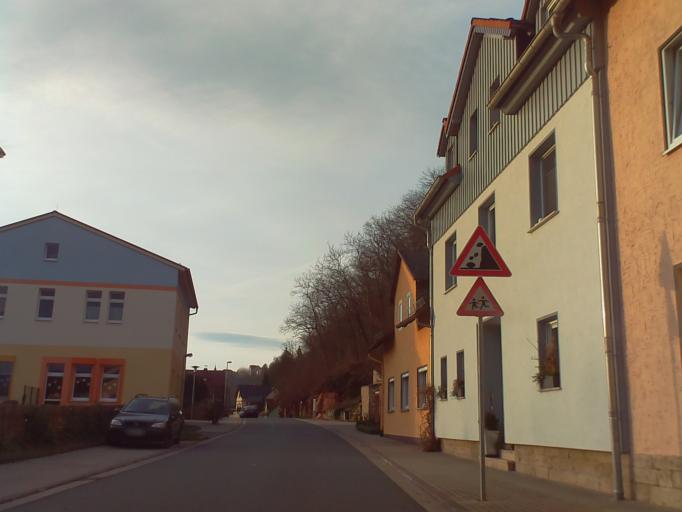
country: DE
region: Thuringia
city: Freienorla
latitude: 50.7755
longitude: 11.5395
